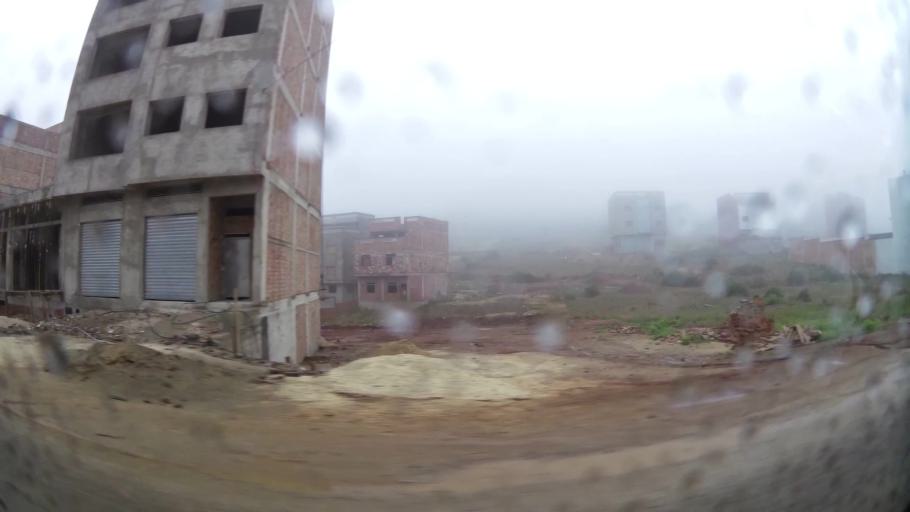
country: MA
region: Taza-Al Hoceima-Taounate
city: Tirhanimine
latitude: 35.2313
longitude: -3.9615
